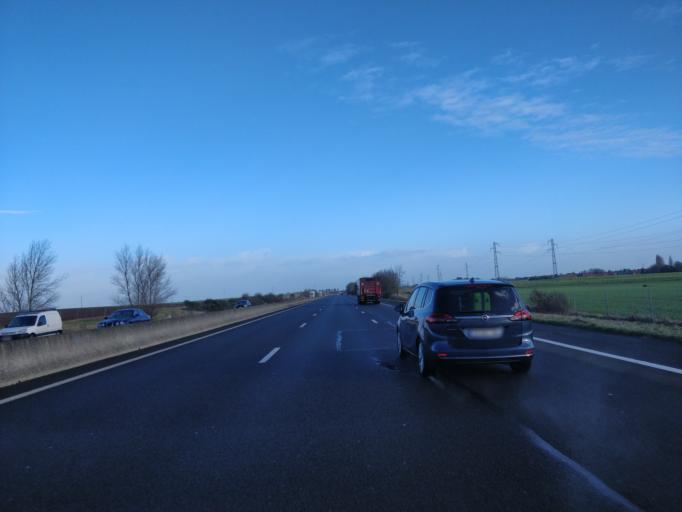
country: FR
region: Centre
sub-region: Departement du Loiret
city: Beaugency
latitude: 47.7982
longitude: 1.6121
